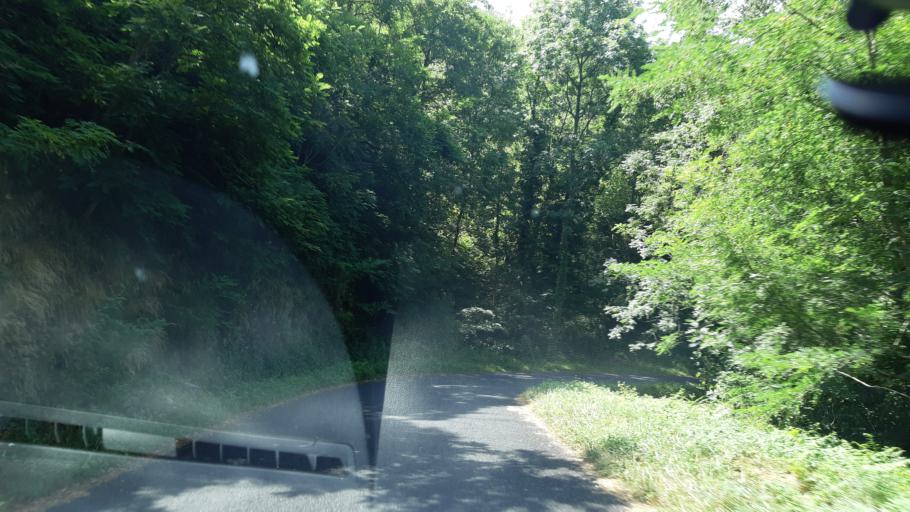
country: FR
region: Languedoc-Roussillon
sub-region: Departement des Pyrenees-Orientales
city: Arles
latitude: 42.5227
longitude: 2.6191
